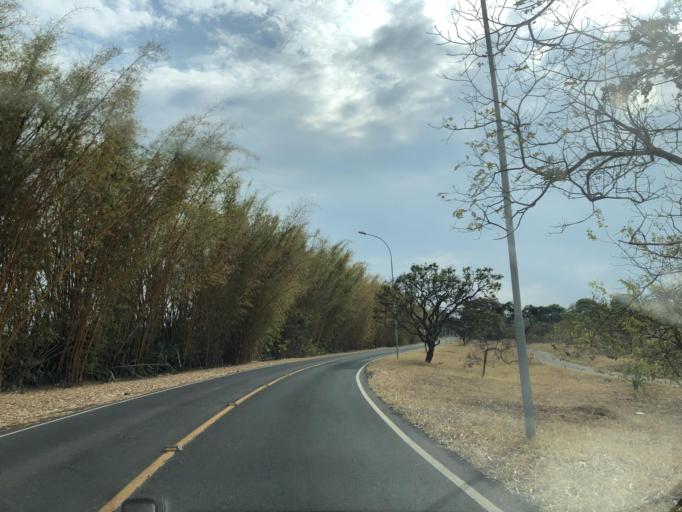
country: BR
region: Federal District
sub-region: Brasilia
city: Brasilia
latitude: -15.9436
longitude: -47.9824
